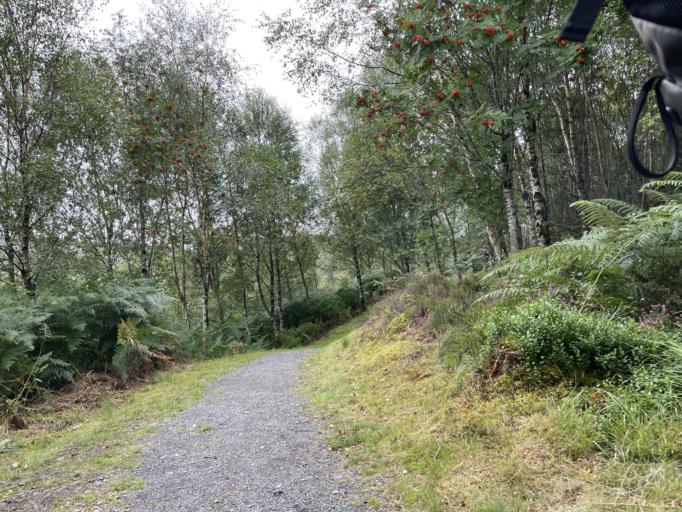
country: GB
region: Scotland
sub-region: Dumfries and Galloway
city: Newton Stewart
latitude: 55.0815
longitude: -4.5088
